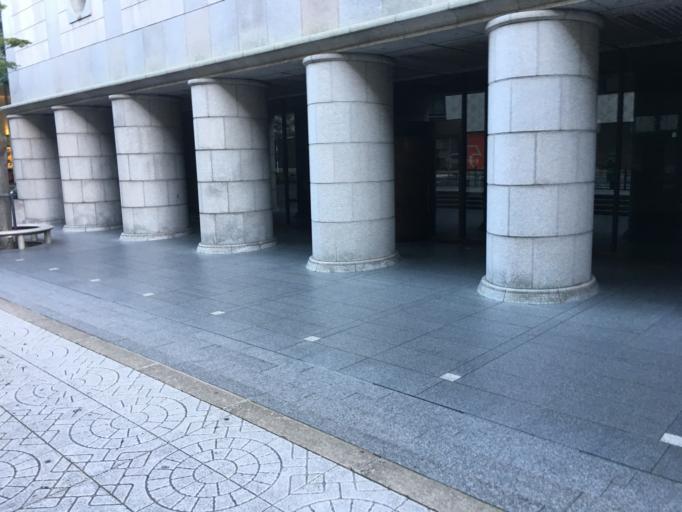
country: JP
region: Osaka
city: Osaka-shi
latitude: 34.6816
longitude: 135.5051
